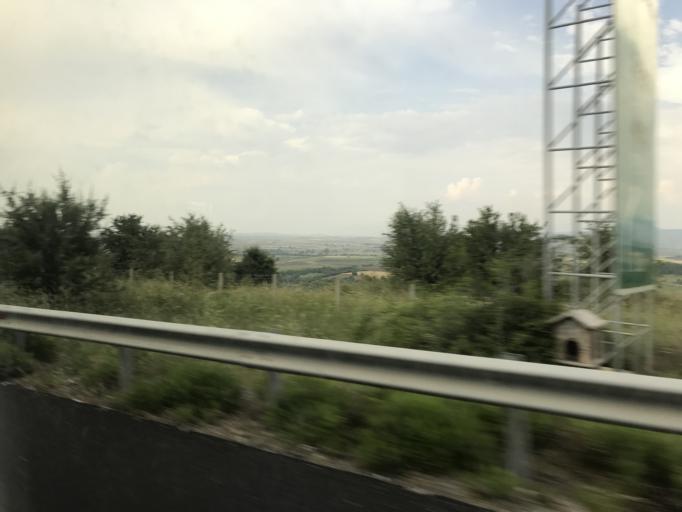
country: GR
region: East Macedonia and Thrace
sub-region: Nomos Rodopis
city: Sapes
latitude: 40.9528
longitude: 25.6571
